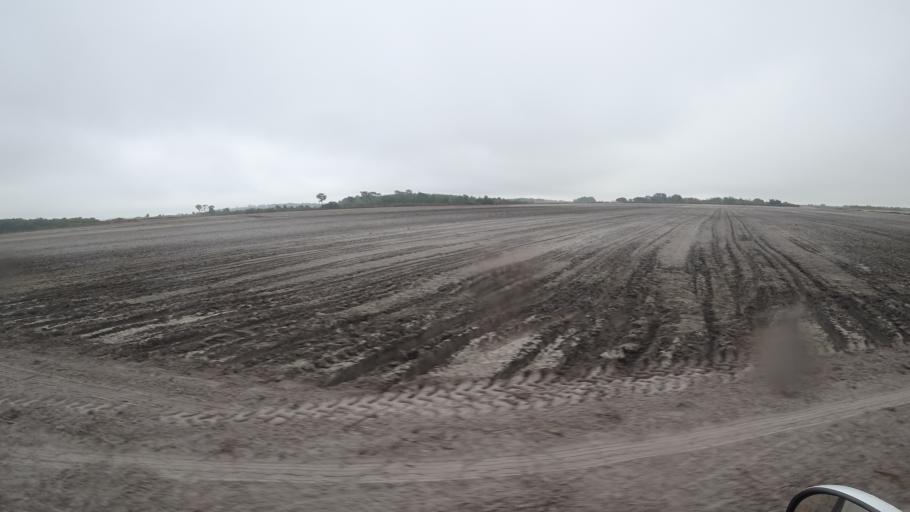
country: US
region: Florida
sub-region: Sarasota County
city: Warm Mineral Springs
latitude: 27.2989
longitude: -82.1666
